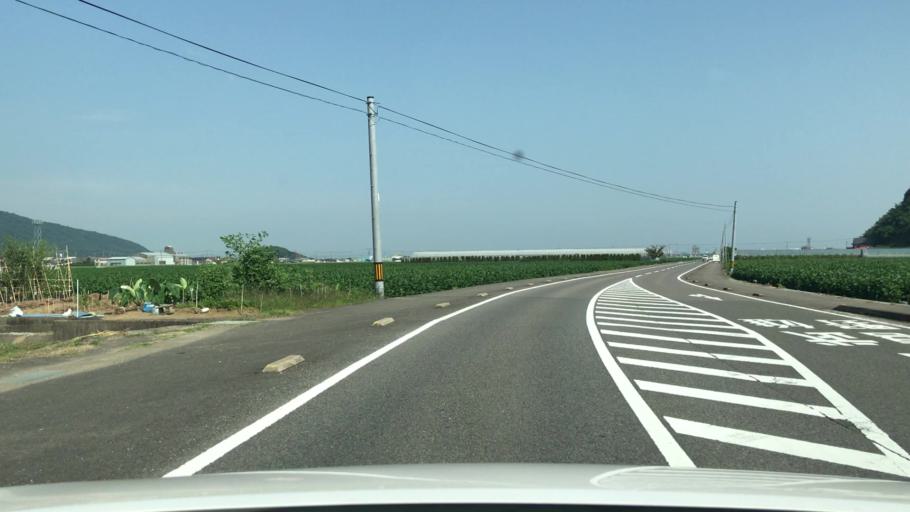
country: JP
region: Saga Prefecture
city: Kashima
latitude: 33.1213
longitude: 130.0643
